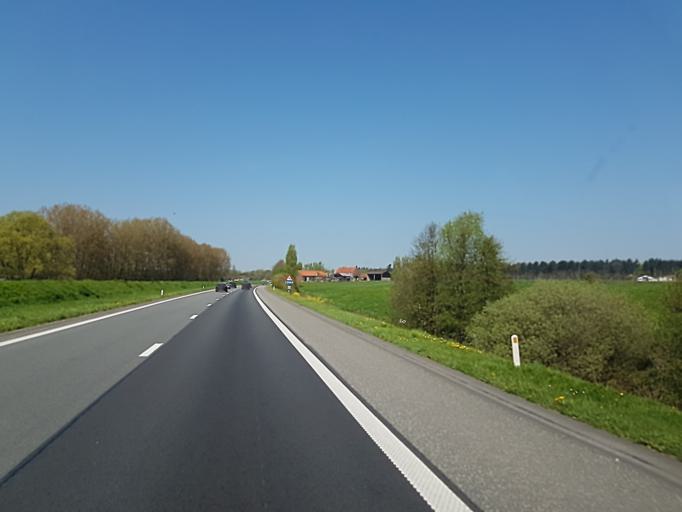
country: BE
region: Flanders
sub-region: Provincie West-Vlaanderen
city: Zonnebeke
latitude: 50.8434
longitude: 2.9884
